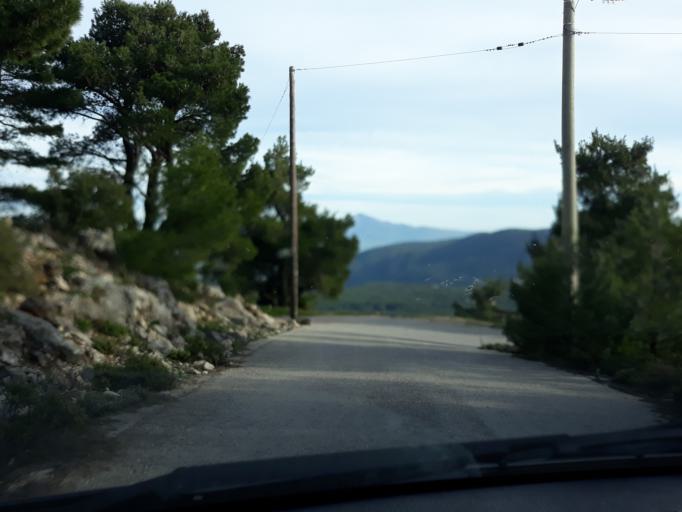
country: GR
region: Attica
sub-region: Nomarchia Anatolikis Attikis
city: Afidnes
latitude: 38.2158
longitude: 23.8047
